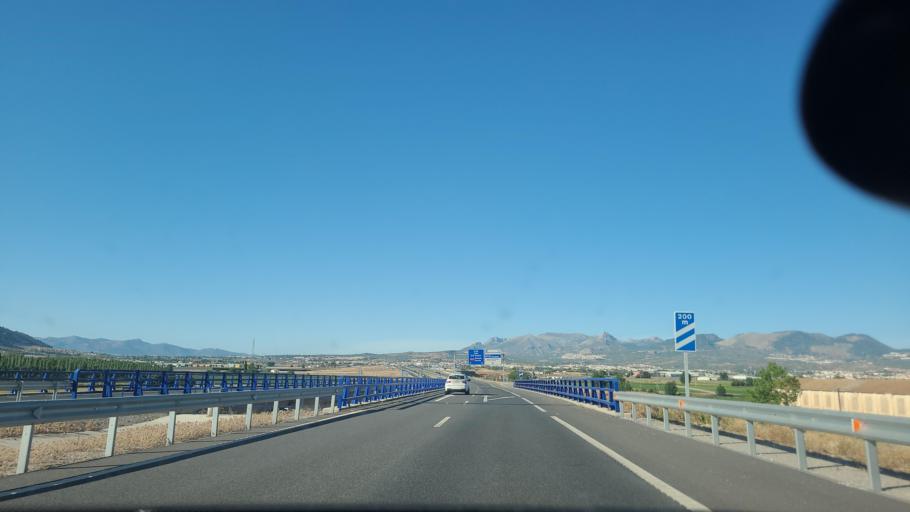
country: ES
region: Andalusia
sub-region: Provincia de Granada
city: Atarfe
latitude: 37.1960
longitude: -3.6845
